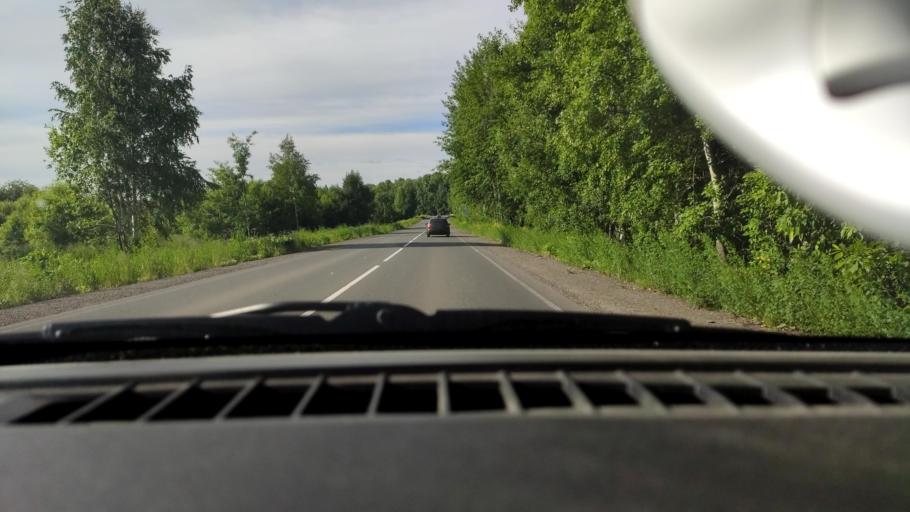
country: RU
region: Perm
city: Nytva
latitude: 57.9269
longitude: 55.4497
